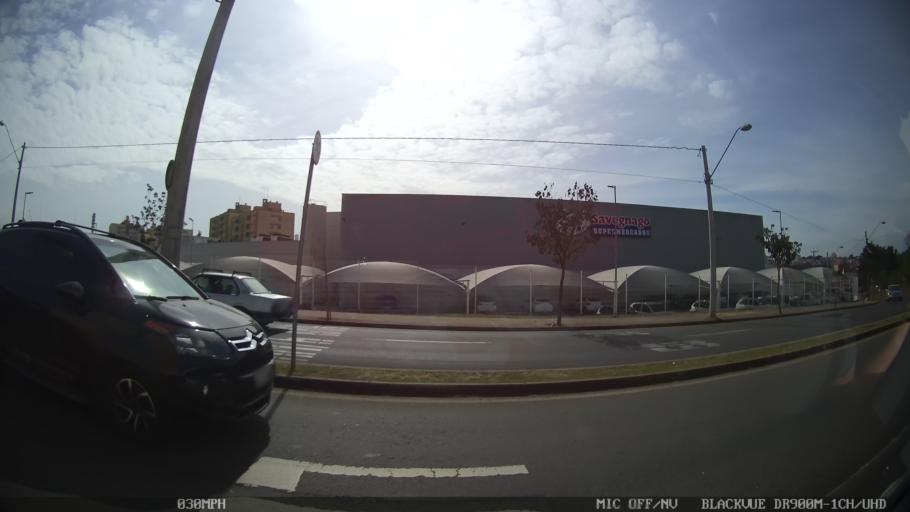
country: BR
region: Sao Paulo
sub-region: Piracicaba
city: Piracicaba
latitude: -22.7475
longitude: -47.6346
